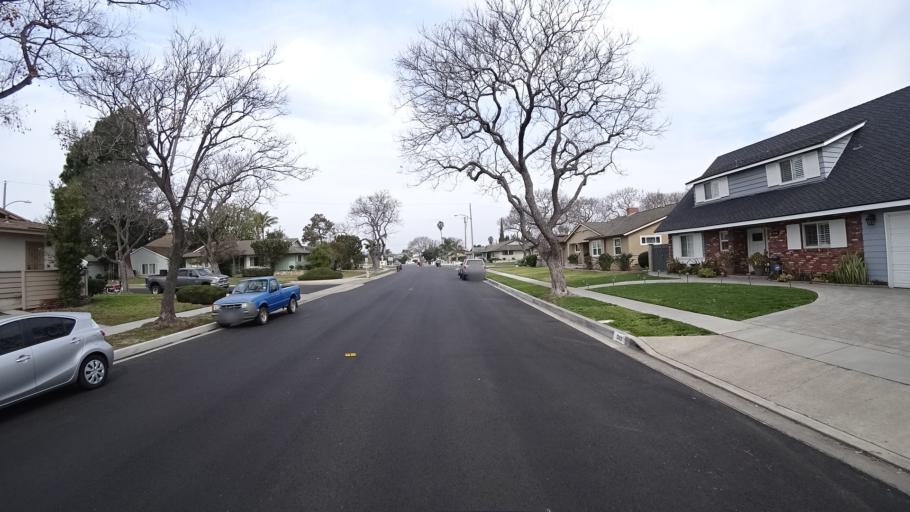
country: US
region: California
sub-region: Orange County
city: Anaheim
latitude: 33.8162
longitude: -117.9446
